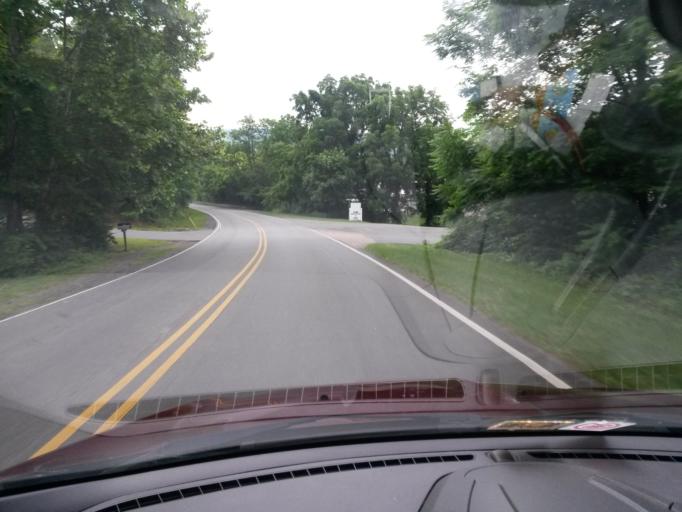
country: US
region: Virginia
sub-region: City of Covington
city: Fairlawn
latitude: 37.7703
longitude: -79.9698
